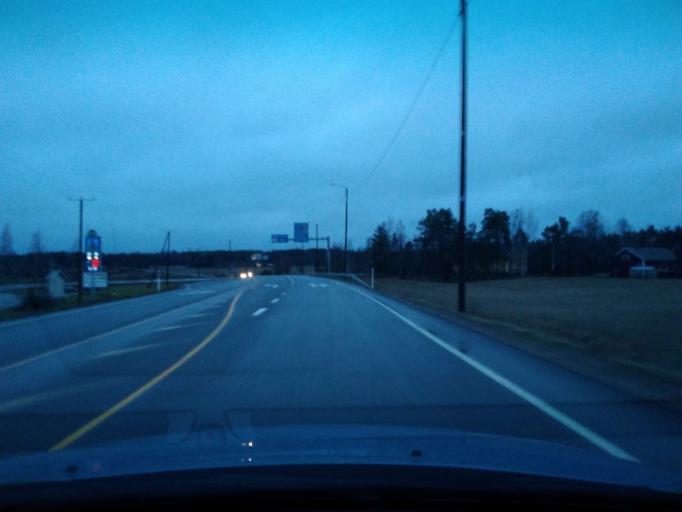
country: FI
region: Uusimaa
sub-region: Porvoo
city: Askola
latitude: 60.4953
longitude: 25.5545
